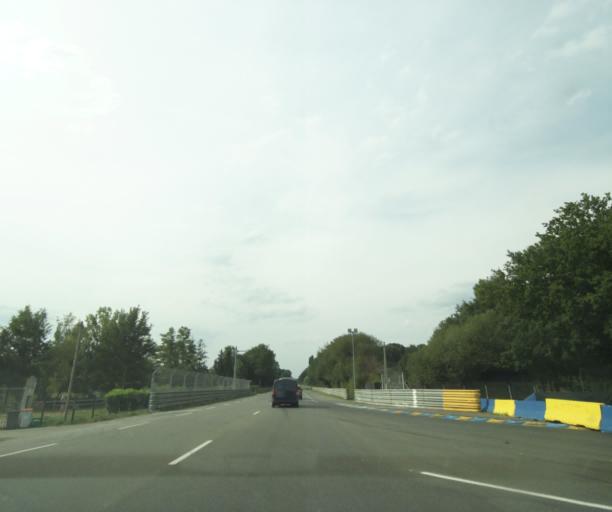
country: FR
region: Pays de la Loire
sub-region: Departement de la Sarthe
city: Mulsanne
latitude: 47.9282
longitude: 0.2414
